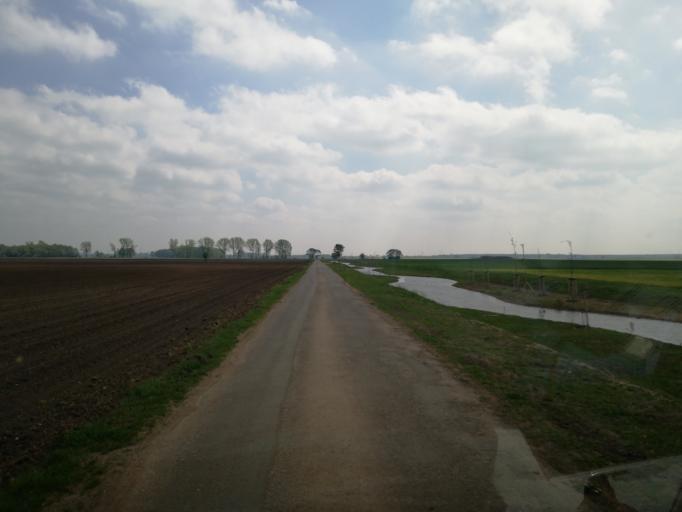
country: DE
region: Brandenburg
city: Doberlug-Kirchhain
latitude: 51.6830
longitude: 13.5341
